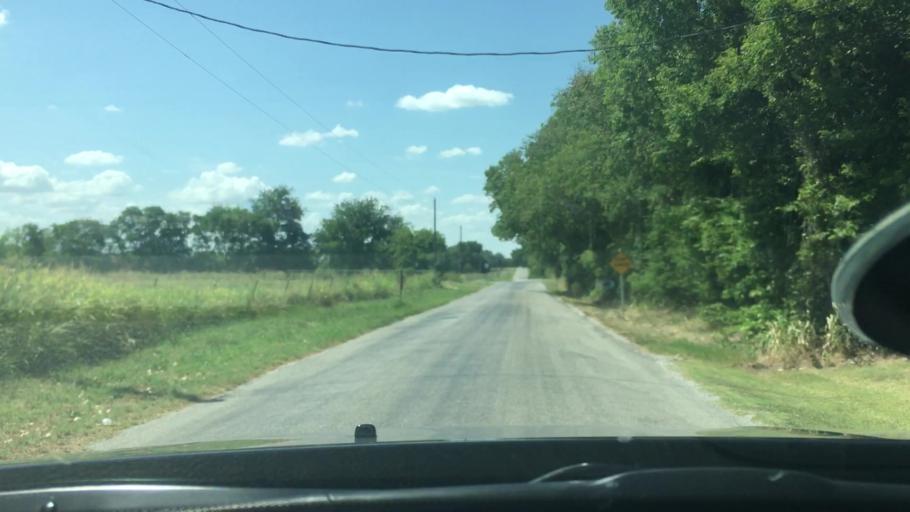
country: US
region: Oklahoma
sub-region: Love County
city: Marietta
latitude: 33.9273
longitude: -97.1608
